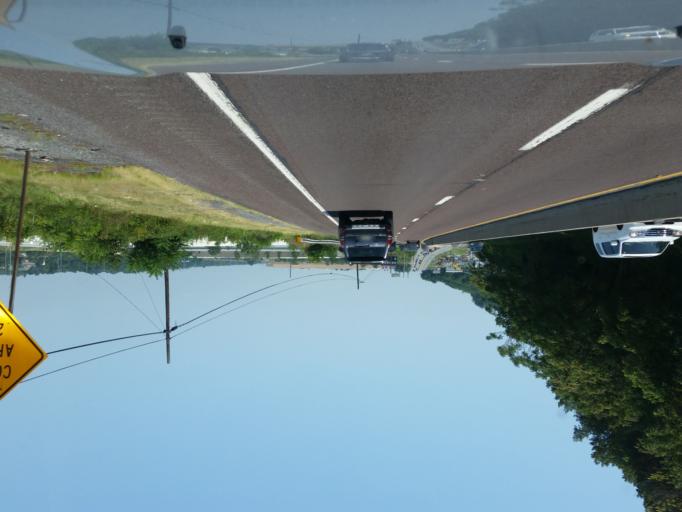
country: US
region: Pennsylvania
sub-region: Dauphin County
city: Rutherford
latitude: 40.2620
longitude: -76.7577
